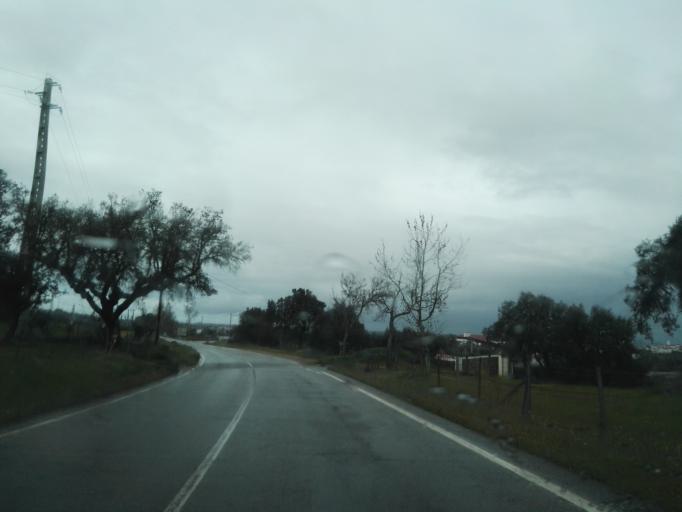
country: PT
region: Portalegre
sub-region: Arronches
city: Arronches
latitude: 39.1122
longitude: -7.2828
